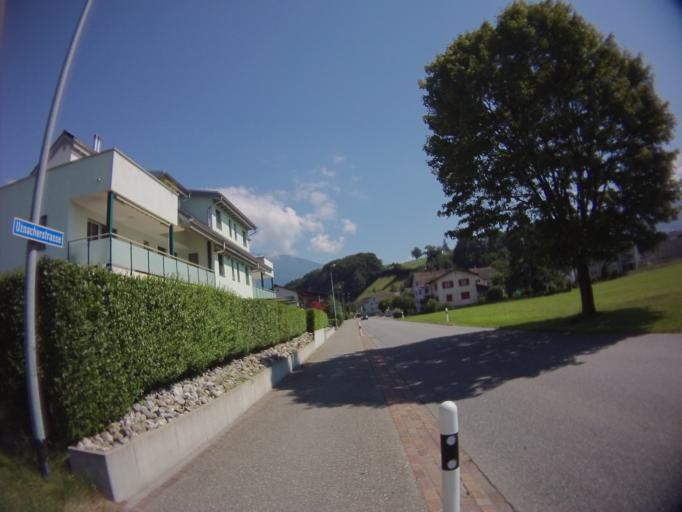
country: CH
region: Saint Gallen
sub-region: Wahlkreis See-Gaster
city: Benken
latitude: 47.2058
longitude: 9.0063
